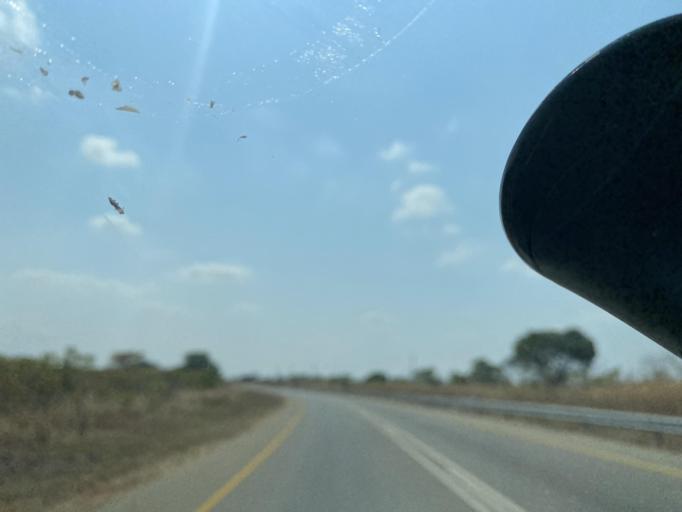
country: ZM
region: Lusaka
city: Chongwe
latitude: -15.5358
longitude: 28.6497
